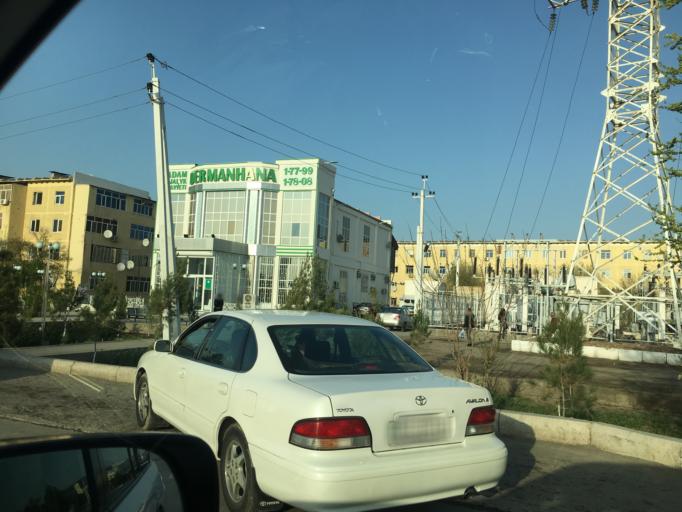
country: TM
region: Lebap
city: Turkmenabat
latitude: 39.0557
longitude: 63.5811
